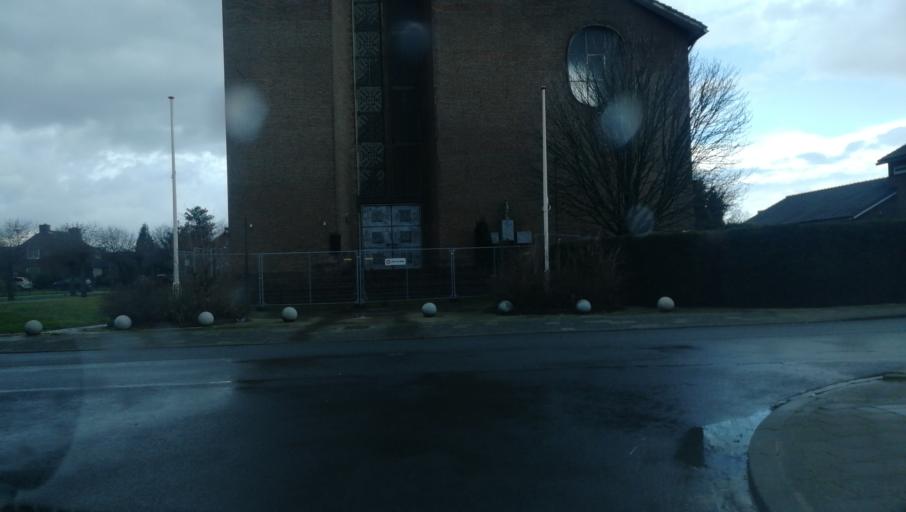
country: NL
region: Limburg
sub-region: Gemeente Venlo
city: Tegelen
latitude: 51.3441
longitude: 6.1469
